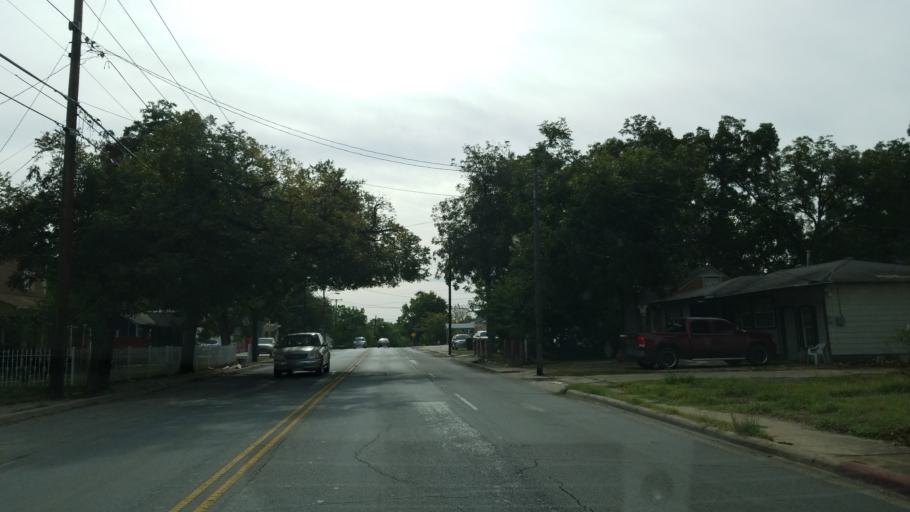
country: US
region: Texas
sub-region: Dallas County
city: Dallas
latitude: 32.7817
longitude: -96.7196
